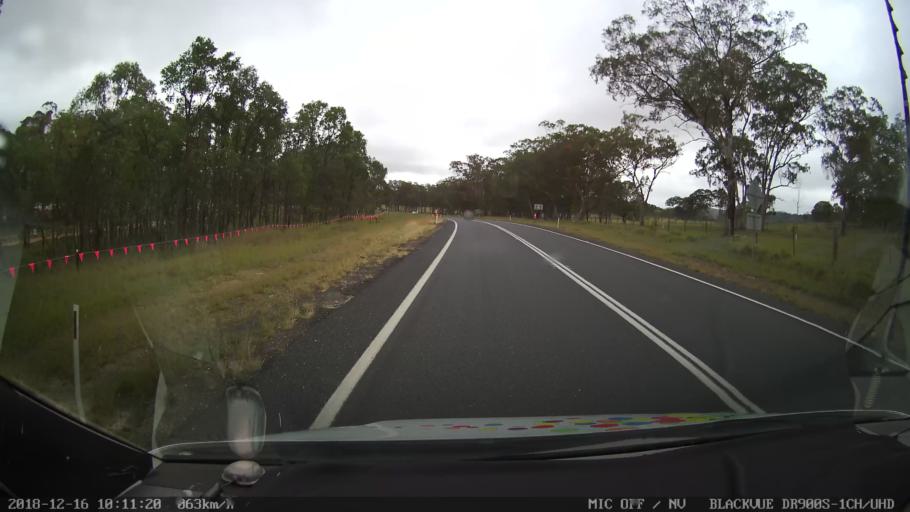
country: AU
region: New South Wales
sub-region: Glen Innes Severn
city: Glen Innes
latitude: -29.3137
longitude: 151.9318
